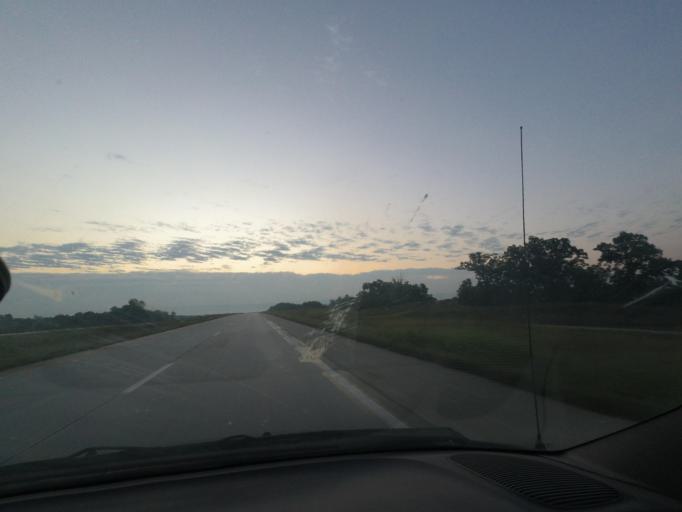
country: US
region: Missouri
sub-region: Linn County
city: Marceline
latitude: 39.7591
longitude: -92.8282
